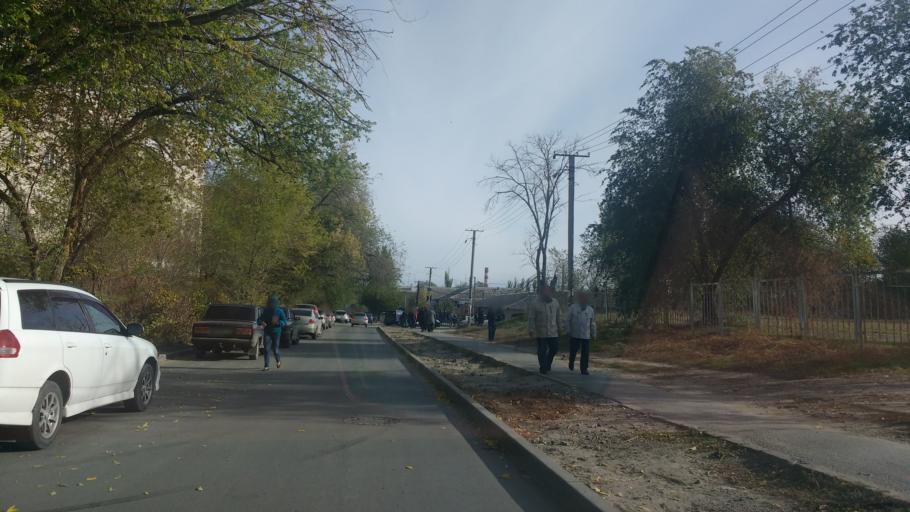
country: RU
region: Volgograd
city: Krasnoslobodsk
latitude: 48.7669
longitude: 44.5506
